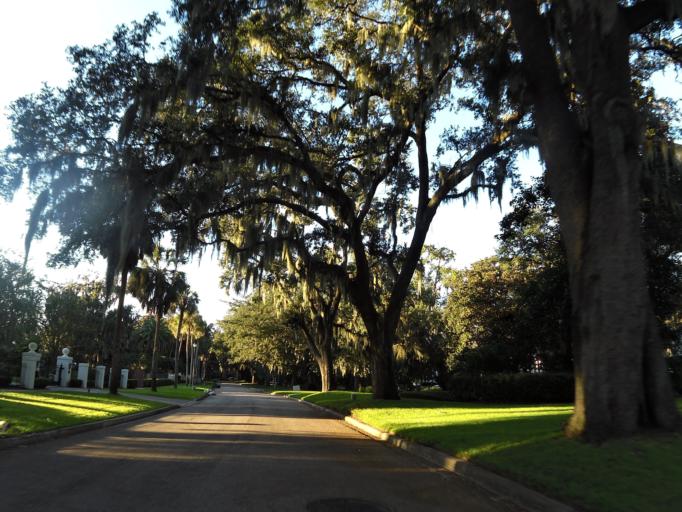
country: US
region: Florida
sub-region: Duval County
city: Jacksonville
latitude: 30.2986
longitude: -81.6541
